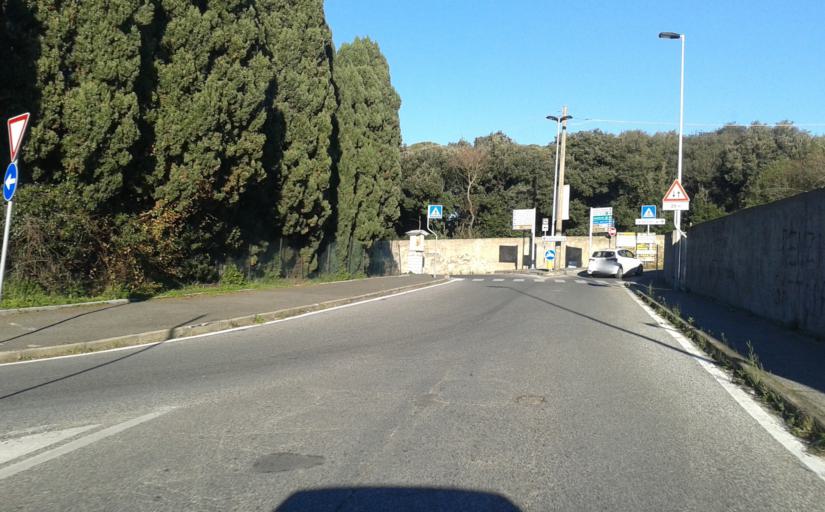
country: IT
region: Tuscany
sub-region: Provincia di Livorno
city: Livorno
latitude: 43.5121
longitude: 10.3269
